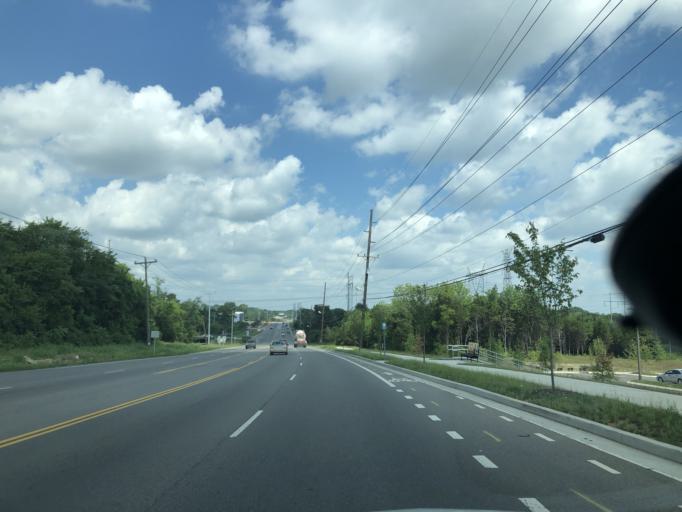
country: US
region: Tennessee
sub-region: Rutherford County
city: La Vergne
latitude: 36.0434
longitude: -86.6069
